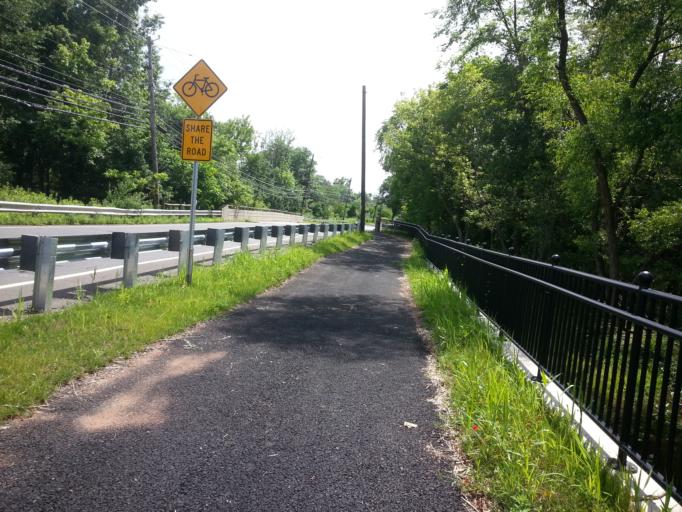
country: US
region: New Jersey
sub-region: Mercer County
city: Pennington
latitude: 40.3321
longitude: -74.7771
